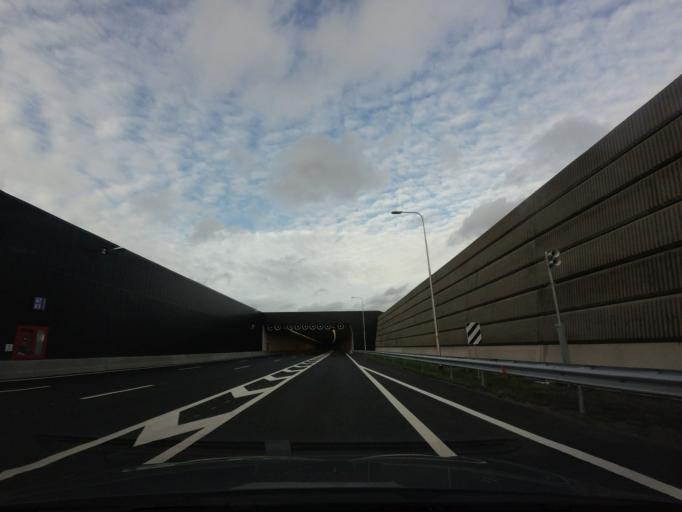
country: NL
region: South Holland
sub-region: Gemeente Schiedam
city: Schiedam
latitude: 51.9307
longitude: 4.3649
